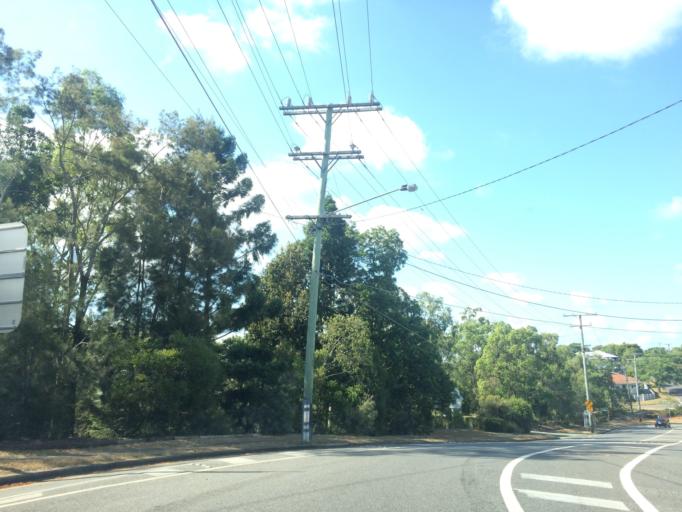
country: AU
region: Queensland
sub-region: Brisbane
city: Seven Hills
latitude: -27.4765
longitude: 153.0664
